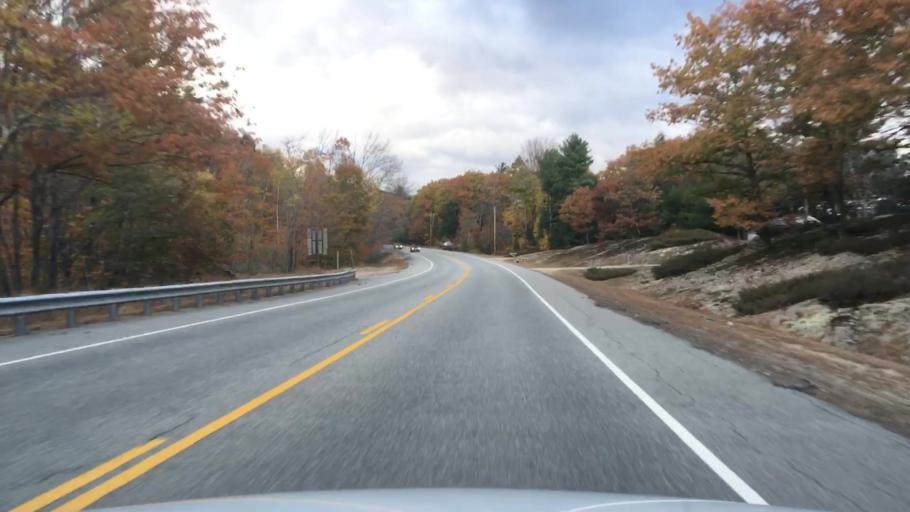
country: US
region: Maine
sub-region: Androscoggin County
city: Livermore
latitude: 44.3904
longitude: -70.2560
